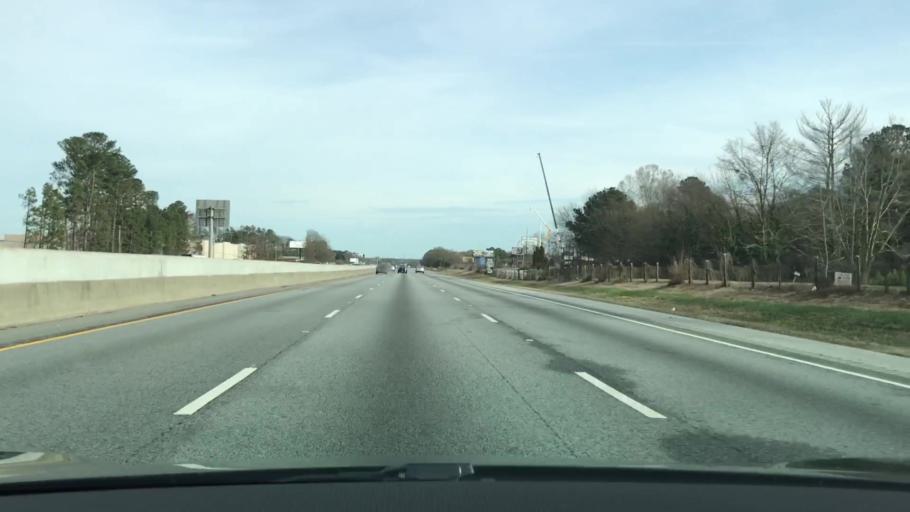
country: US
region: Georgia
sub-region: Rockdale County
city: Conyers
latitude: 33.6313
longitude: -83.9686
